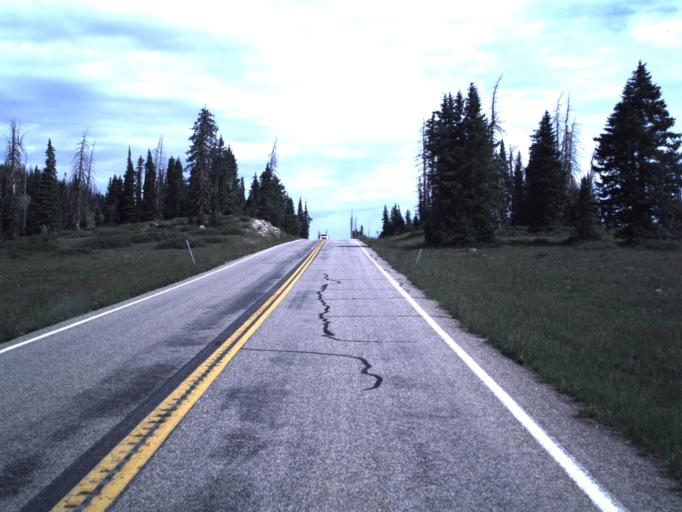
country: US
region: Utah
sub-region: Iron County
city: Cedar City
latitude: 37.5958
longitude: -112.8497
